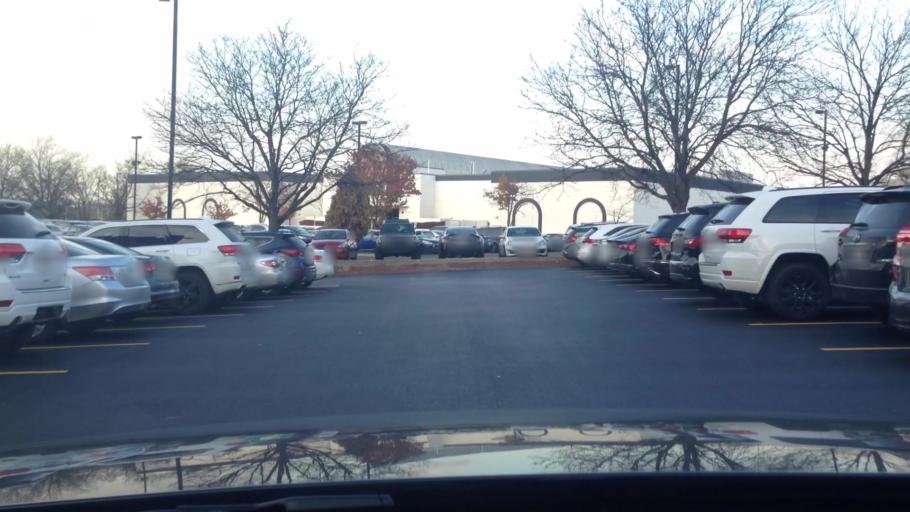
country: US
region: Illinois
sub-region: Cook County
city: Rolling Meadows
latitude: 42.0535
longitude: -88.0012
